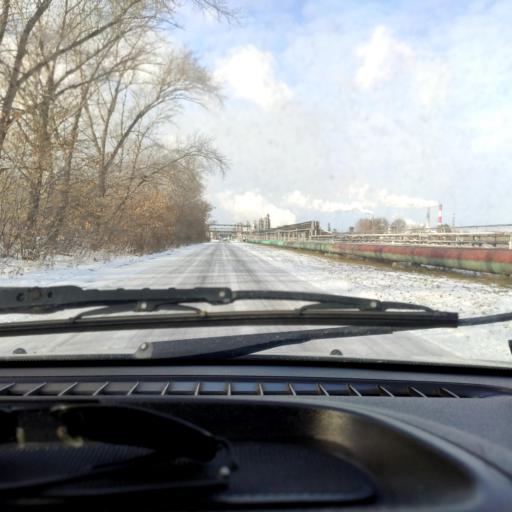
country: RU
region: Samara
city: Tol'yatti
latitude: 53.5349
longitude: 49.4775
